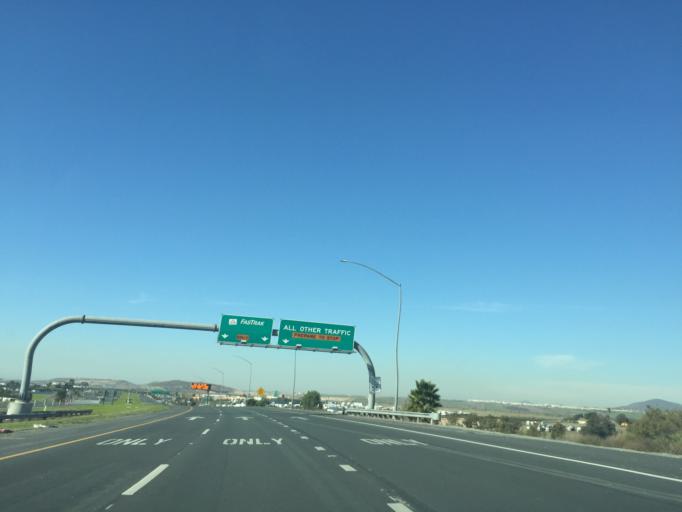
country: MX
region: Baja California
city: Tijuana
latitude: 32.5726
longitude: -116.9510
